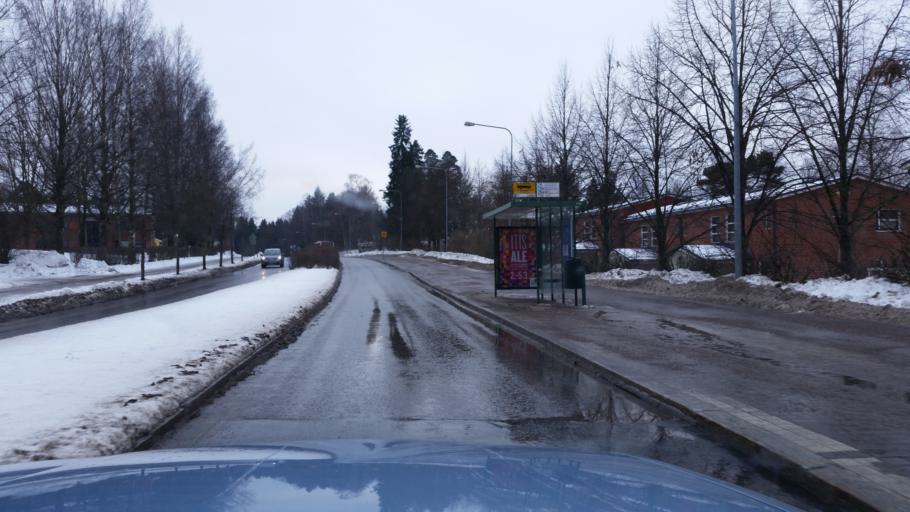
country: FI
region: Uusimaa
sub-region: Helsinki
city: Vantaa
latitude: 60.2668
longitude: 25.0583
